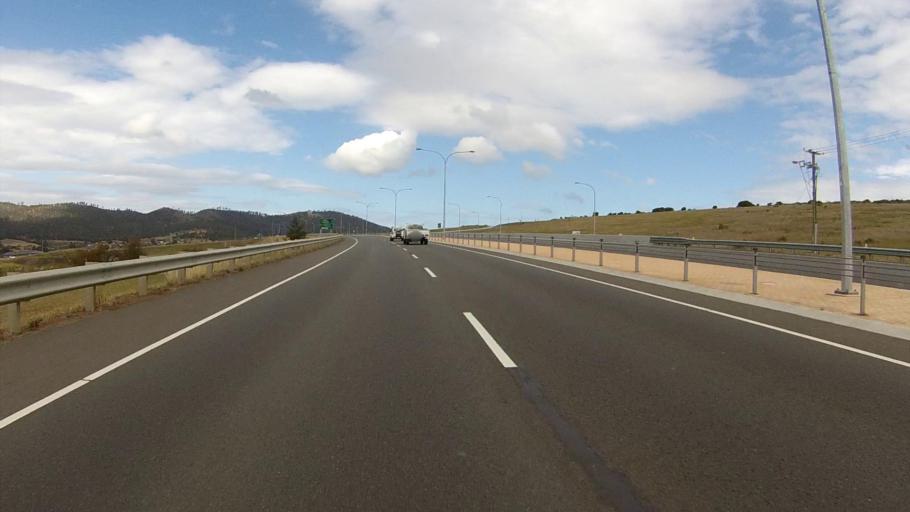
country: AU
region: Tasmania
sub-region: Clarence
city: Howrah
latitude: -42.8883
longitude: 147.4240
